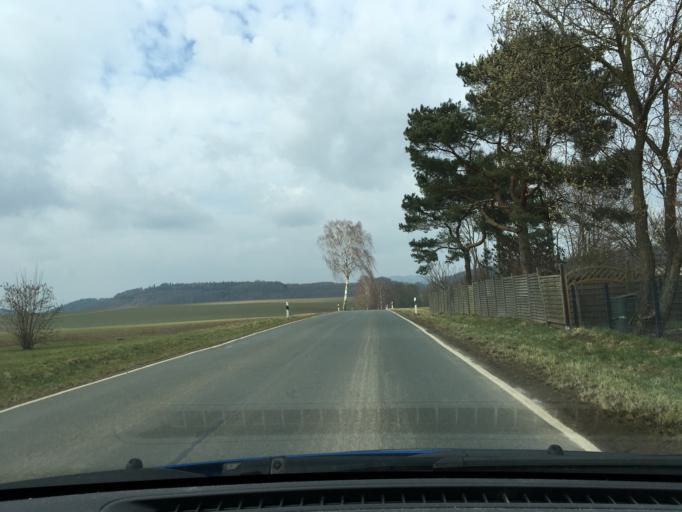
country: DE
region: Lower Saxony
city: Adelebsen
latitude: 51.5417
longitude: 9.7388
